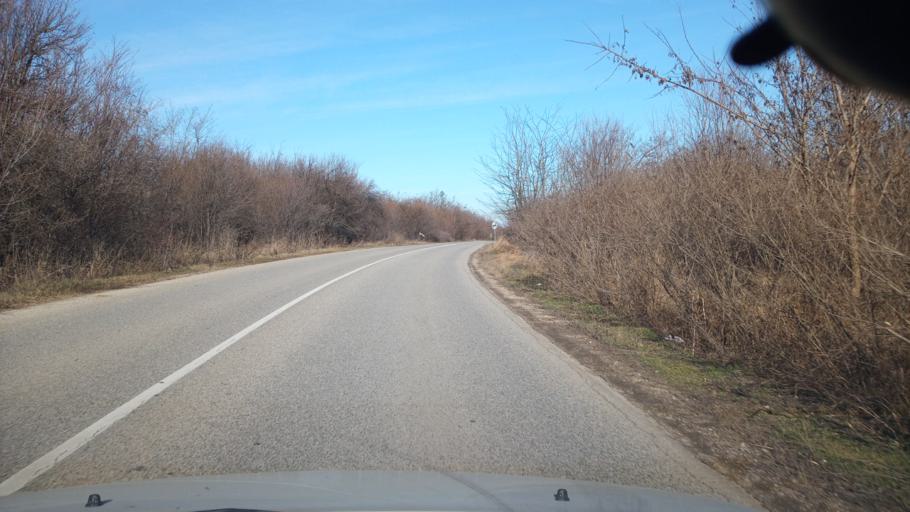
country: BG
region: Pleven
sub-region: Obshtina Pleven
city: Pleven
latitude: 43.4382
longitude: 24.7194
